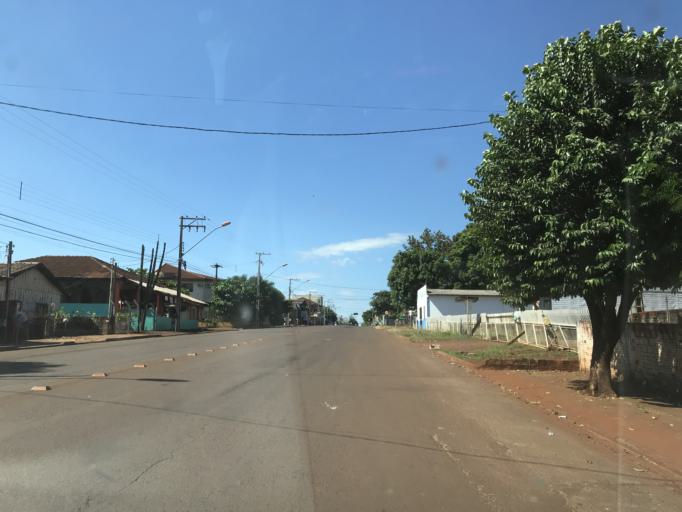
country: BR
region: Parana
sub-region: Palotina
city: Palotina
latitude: -24.2860
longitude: -53.8497
